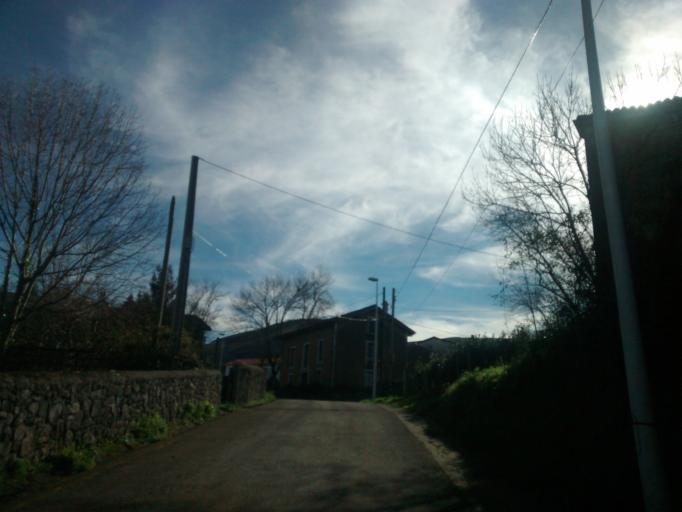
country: ES
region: Cantabria
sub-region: Provincia de Cantabria
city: Entrambasaguas
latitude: 43.3455
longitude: -3.7008
